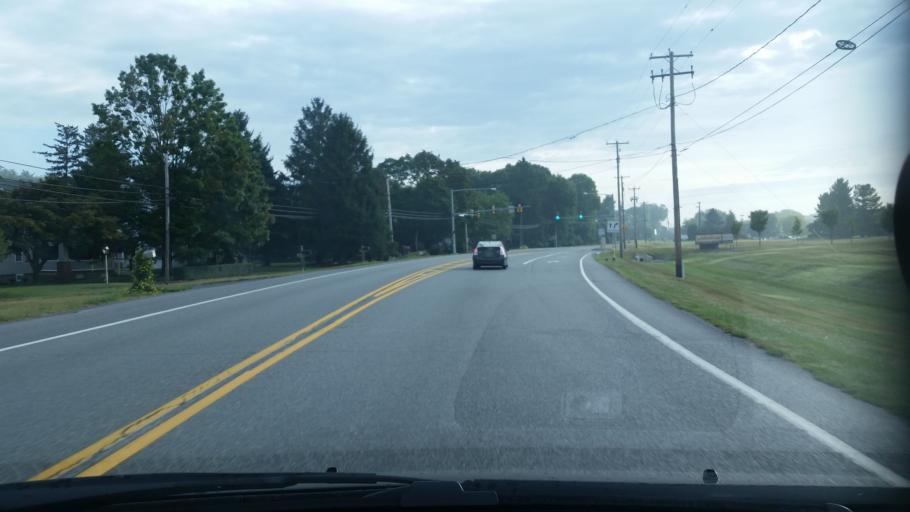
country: US
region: Pennsylvania
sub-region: Lancaster County
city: Brownstown
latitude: 40.0835
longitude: -76.2311
